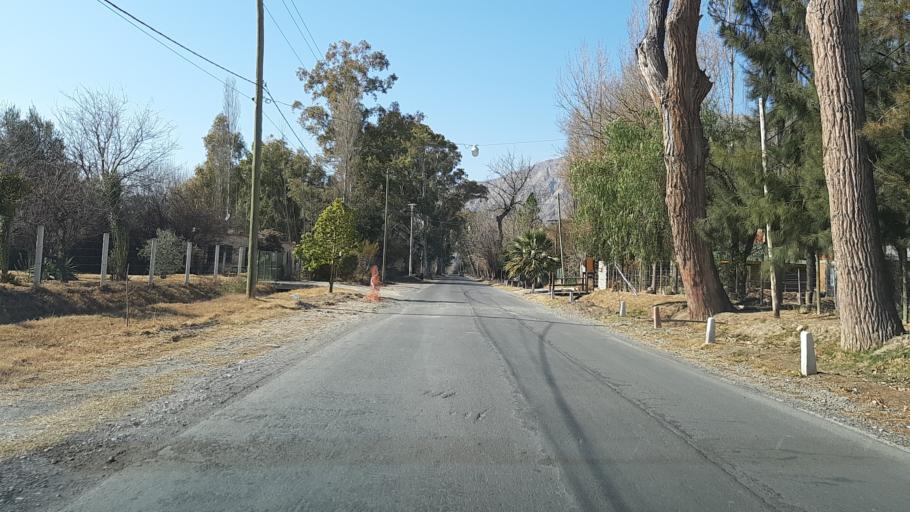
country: AR
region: San Juan
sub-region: Departamento de Zonda
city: Zonda
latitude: -31.5608
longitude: -68.7260
